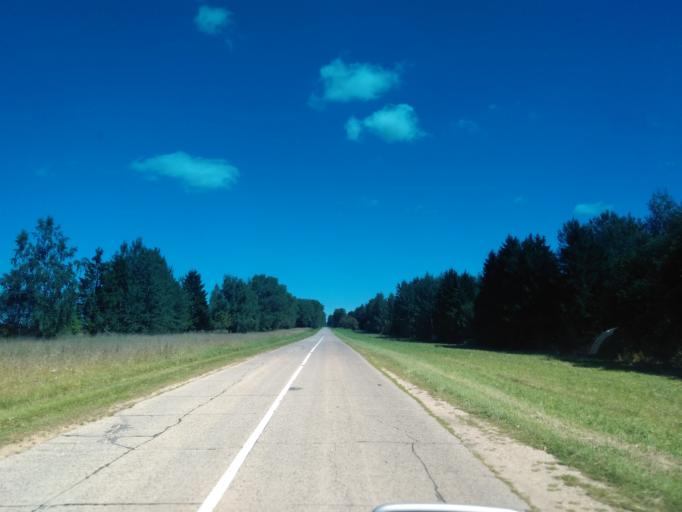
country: BY
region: Minsk
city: Stan'kava
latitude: 53.6489
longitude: 27.3041
